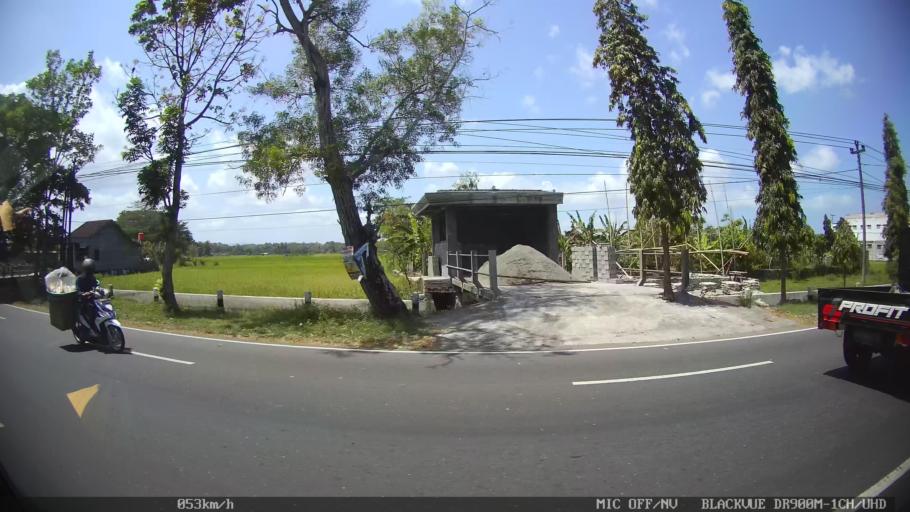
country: ID
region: Daerah Istimewa Yogyakarta
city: Pandak
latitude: -7.9212
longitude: 110.2818
